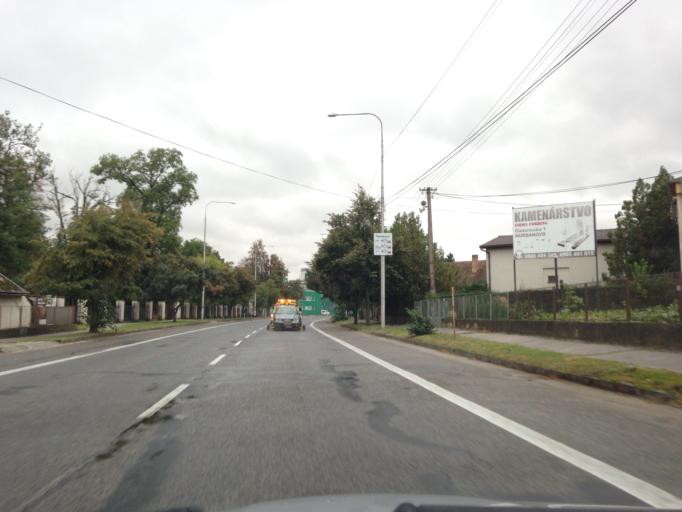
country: SK
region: Nitriansky
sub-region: Okres Komarno
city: Hurbanovo
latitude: 47.8846
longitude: 18.1978
